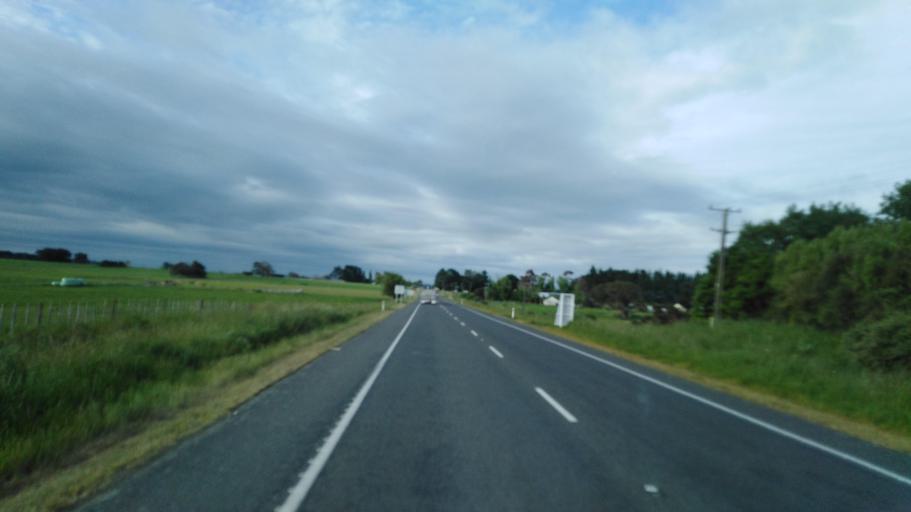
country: NZ
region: Manawatu-Wanganui
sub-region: Rangitikei District
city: Bulls
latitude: -40.2262
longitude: 175.4185
